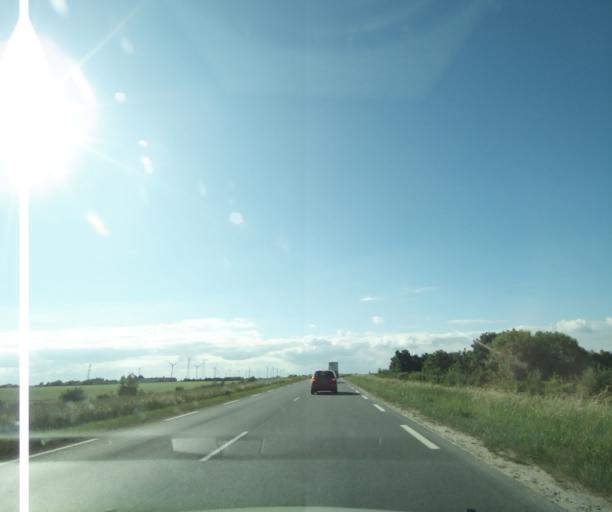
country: FR
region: Centre
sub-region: Departement d'Eure-et-Loir
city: Voves
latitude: 48.2975
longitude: 1.7036
